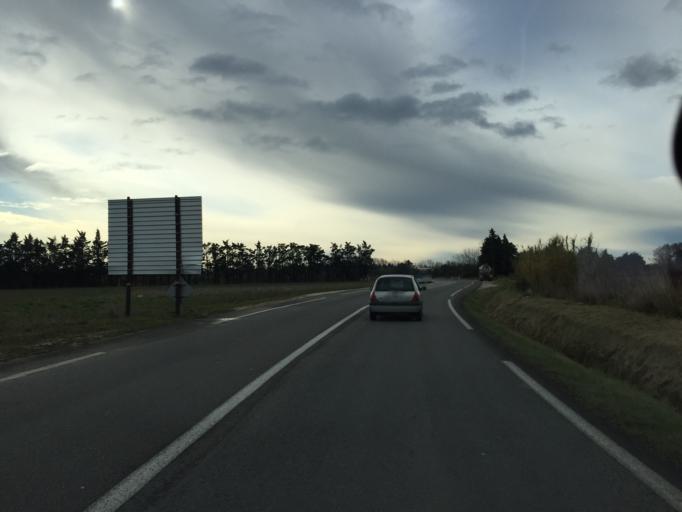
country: FR
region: Provence-Alpes-Cote d'Azur
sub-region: Departement du Vaucluse
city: L'Isle-sur-la-Sorgue
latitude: 43.8952
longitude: 5.0462
